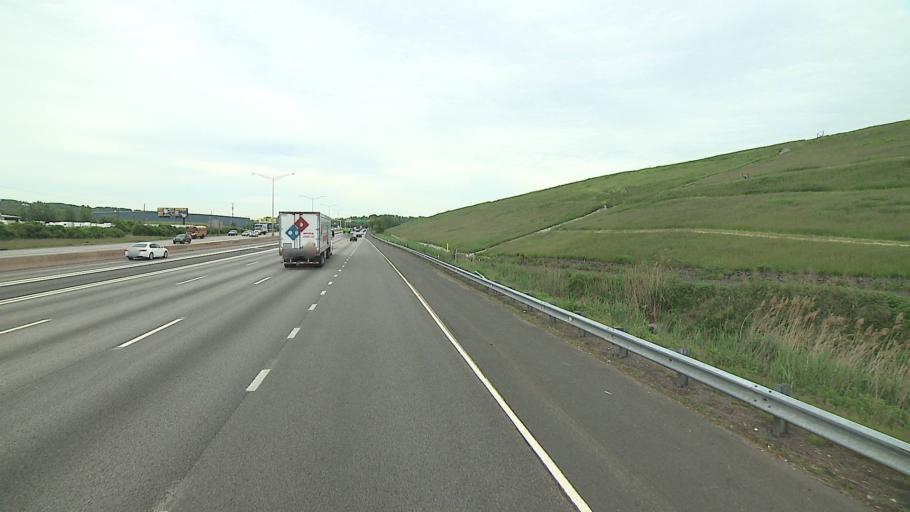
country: US
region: Connecticut
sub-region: Hartford County
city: Hartford
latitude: 41.7915
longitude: -72.6553
